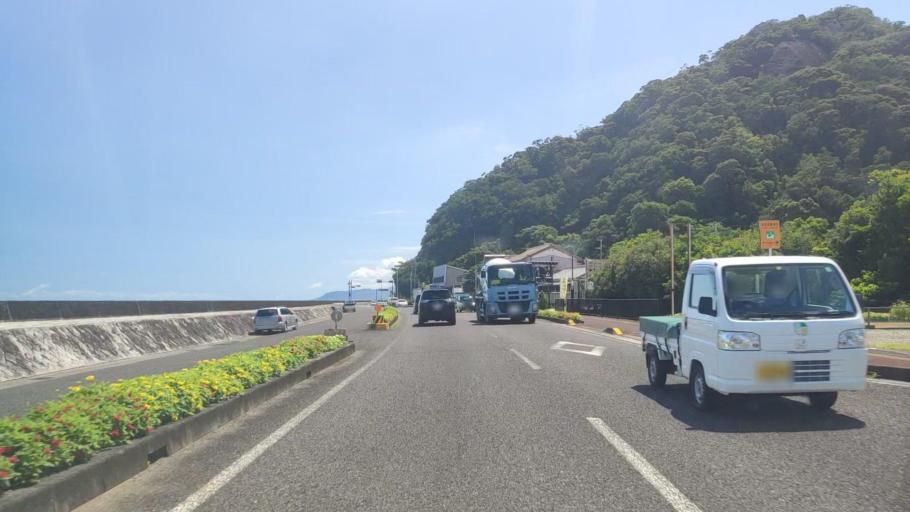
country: JP
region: Wakayama
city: Shingu
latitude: 33.8813
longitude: 136.0951
